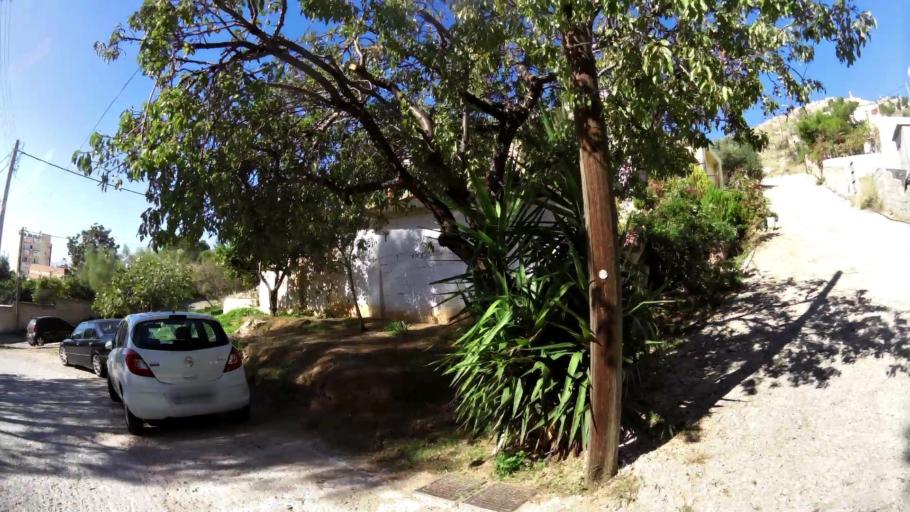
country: GR
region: Attica
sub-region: Nomos Piraios
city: Keratsini
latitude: 37.9642
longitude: 23.5963
